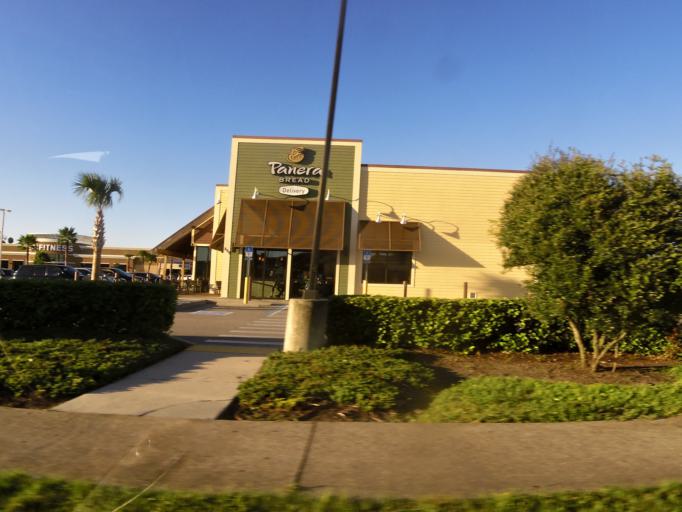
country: US
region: Florida
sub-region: Duval County
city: Atlantic Beach
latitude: 30.3246
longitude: -81.4108
